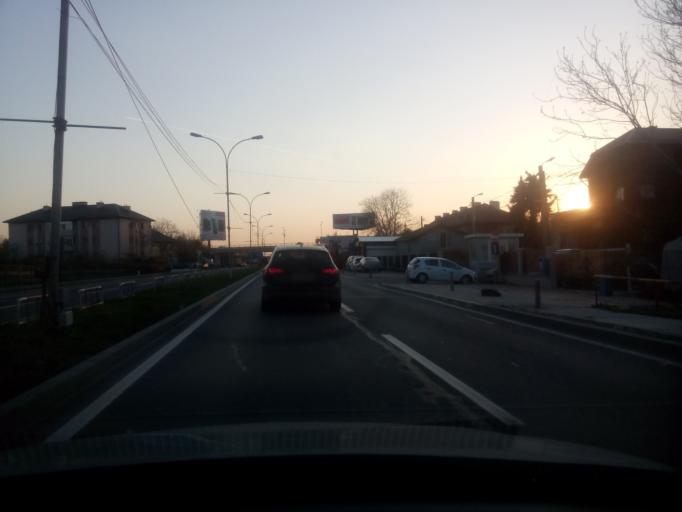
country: RO
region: Ilfov
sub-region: Comuna Otopeni
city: Otopeni
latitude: 44.5733
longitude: 26.0726
